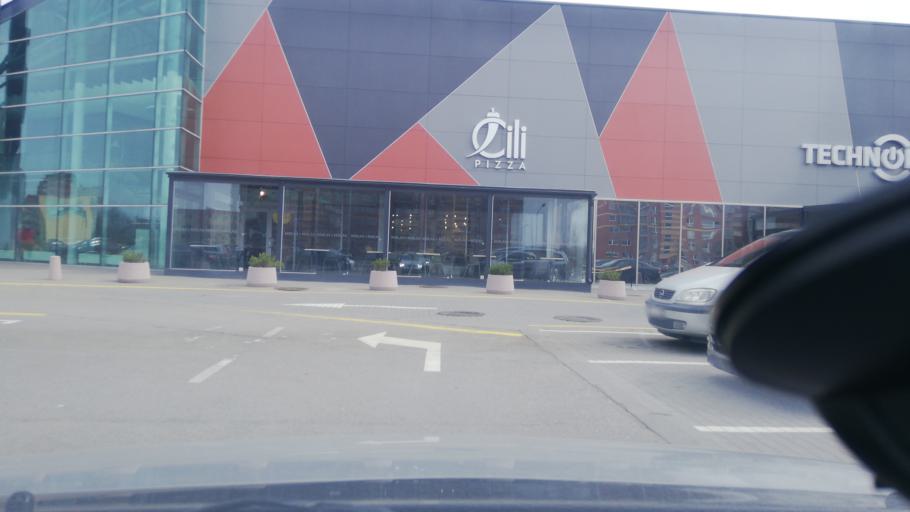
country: LT
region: Klaipedos apskritis
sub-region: Klaipeda
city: Klaipeda
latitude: 55.6647
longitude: 21.1758
